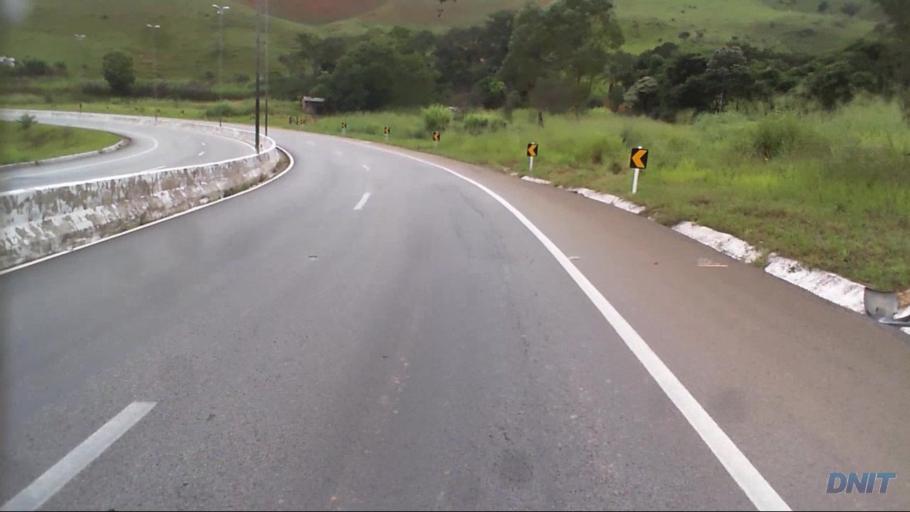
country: BR
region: Minas Gerais
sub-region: Nova Era
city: Nova Era
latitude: -19.7613
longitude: -43.0468
